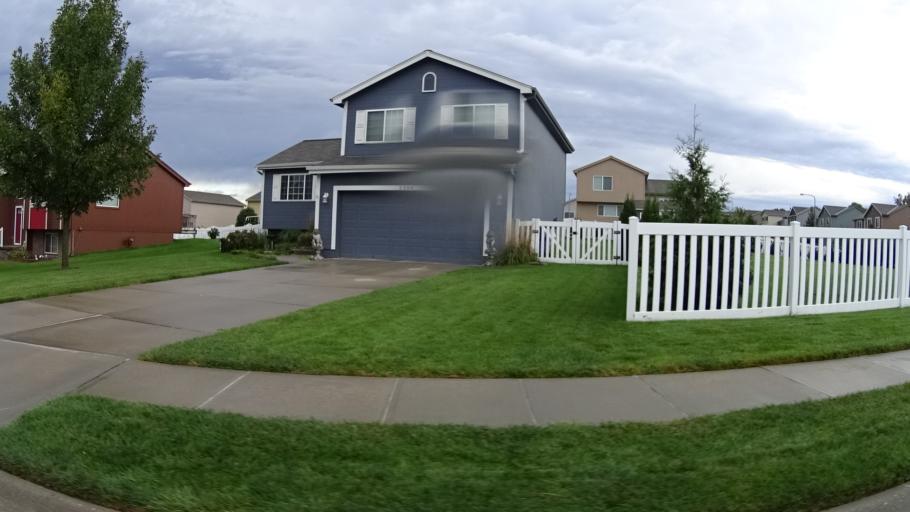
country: US
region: Nebraska
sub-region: Sarpy County
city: Offutt Air Force Base
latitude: 41.1523
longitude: -95.9487
